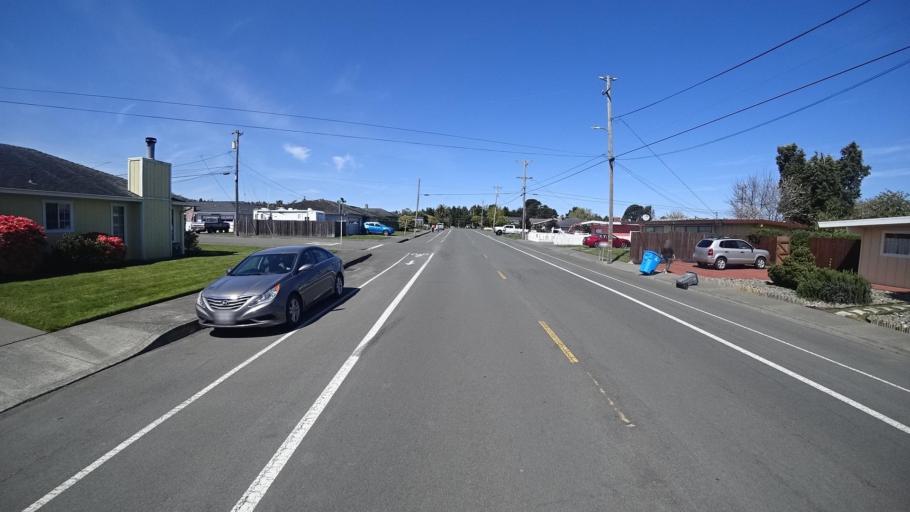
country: US
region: California
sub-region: Humboldt County
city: Myrtletown
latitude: 40.7878
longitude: -124.1280
